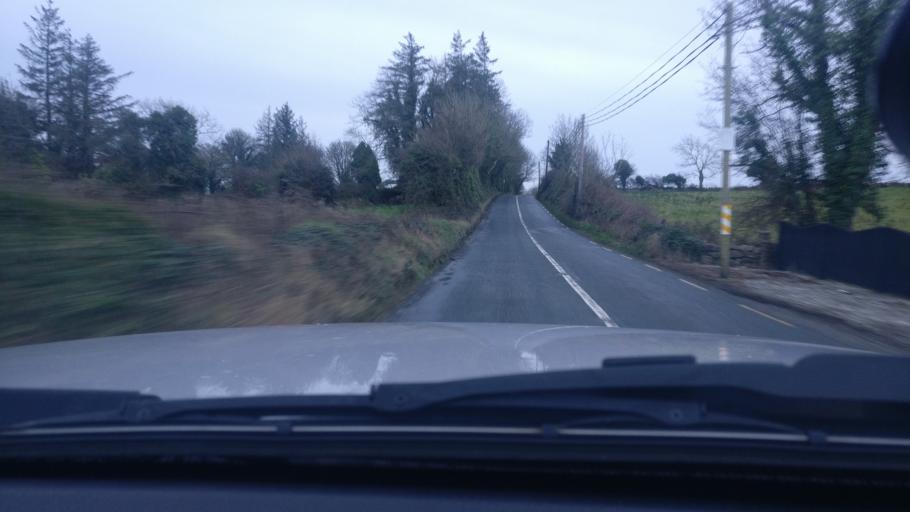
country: IE
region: Connaught
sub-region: County Galway
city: Loughrea
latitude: 53.1673
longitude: -8.5218
